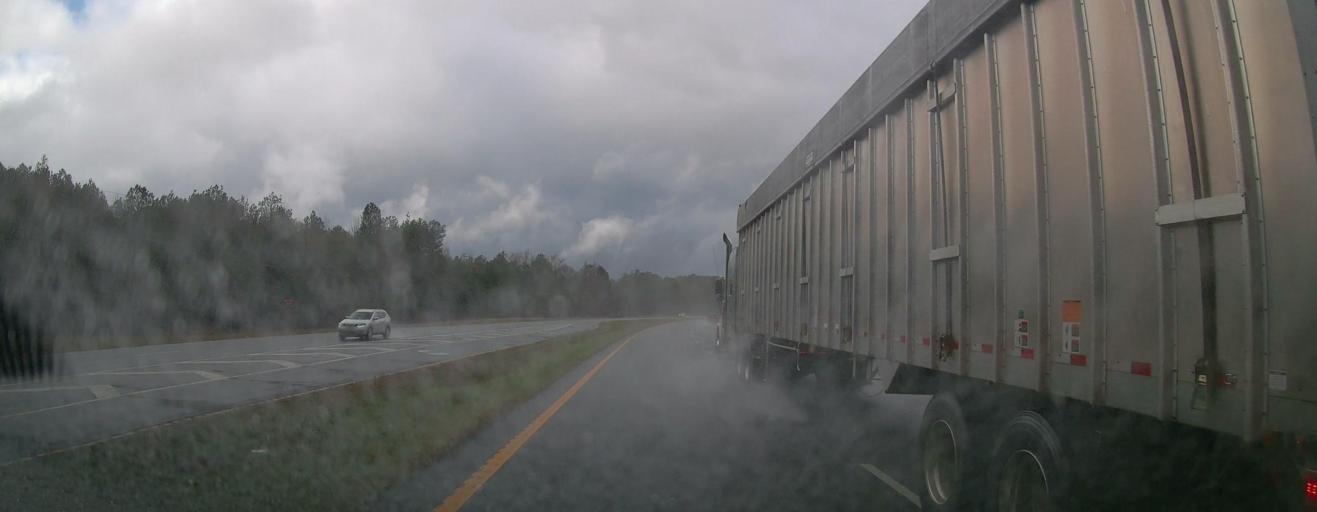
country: US
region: Georgia
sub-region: Clarke County
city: Country Club Estates
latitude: 34.0273
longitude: -83.4004
